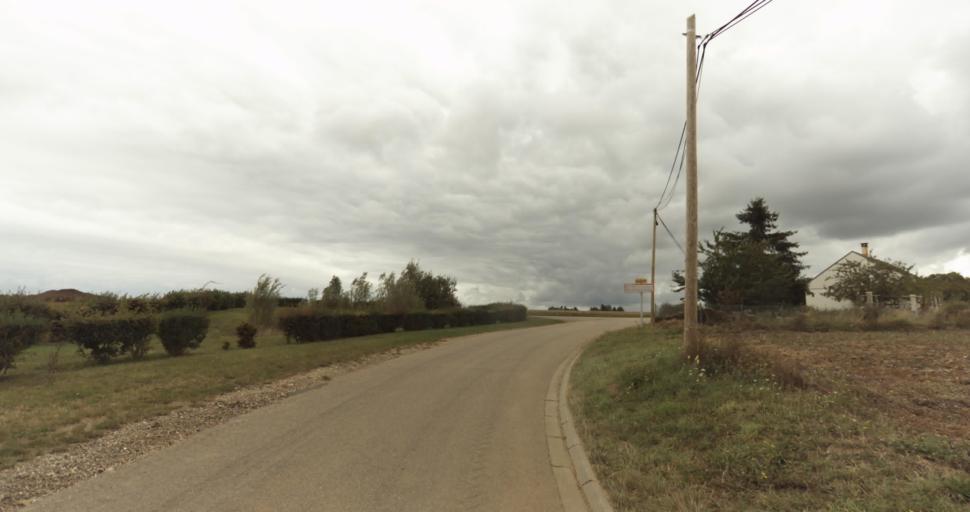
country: FR
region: Haute-Normandie
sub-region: Departement de l'Eure
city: Menilles
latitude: 49.0214
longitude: 1.3011
